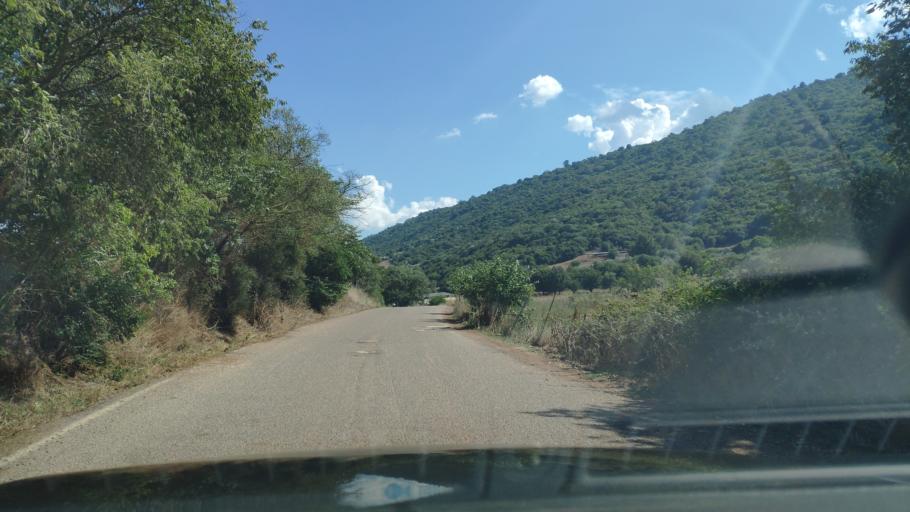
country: GR
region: West Greece
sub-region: Nomos Aitolias kai Akarnanias
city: Katouna
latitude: 38.8454
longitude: 21.0940
